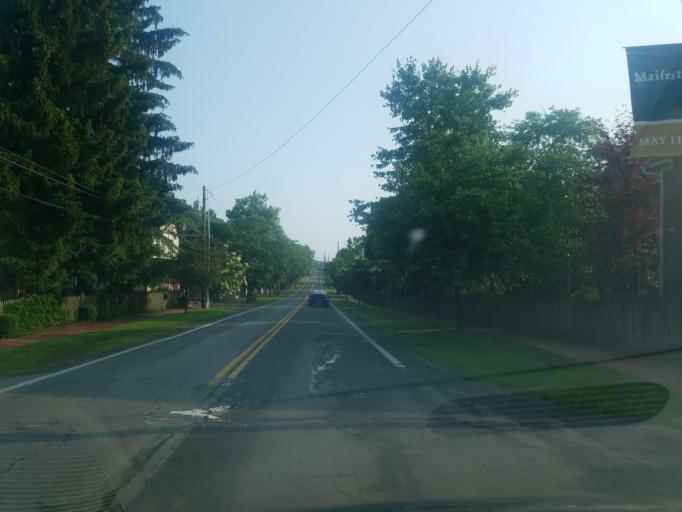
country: US
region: Ohio
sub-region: Tuscarawas County
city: Dover
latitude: 40.6125
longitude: -81.4224
